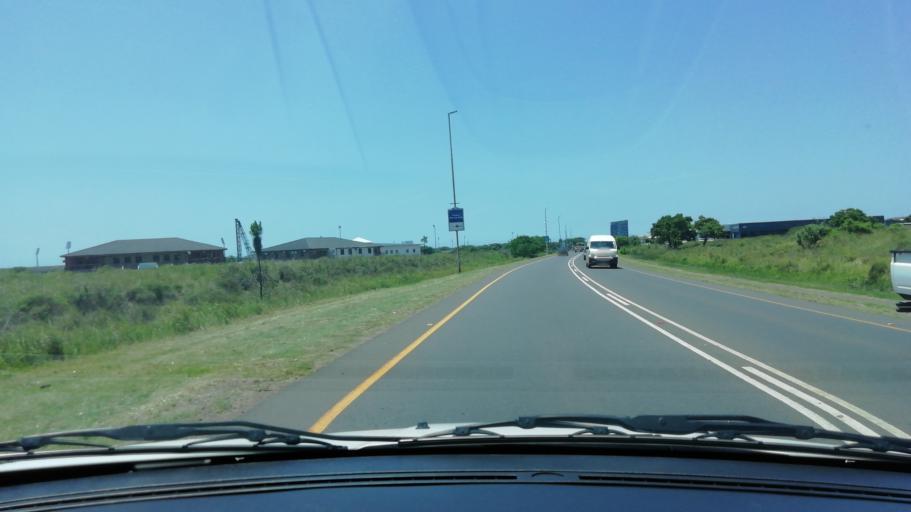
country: ZA
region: KwaZulu-Natal
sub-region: uThungulu District Municipality
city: Richards Bay
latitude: -28.7408
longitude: 32.0481
